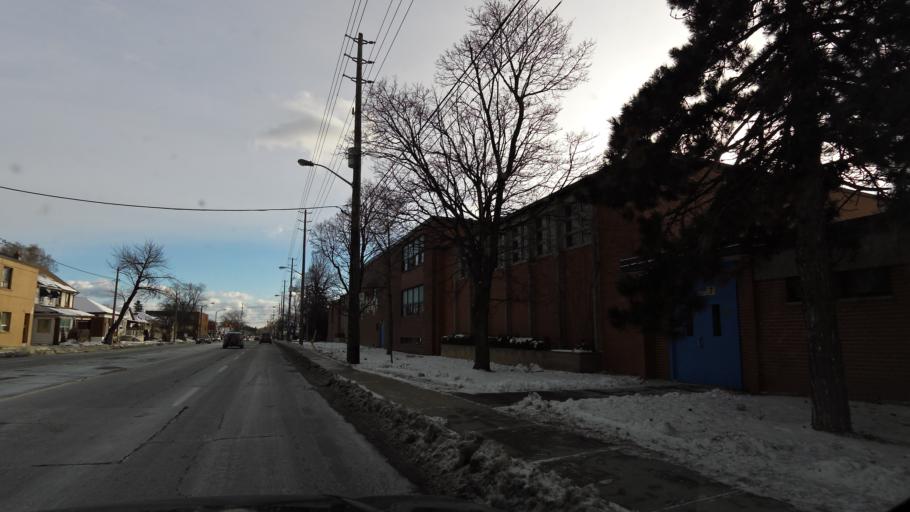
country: CA
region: Ontario
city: Etobicoke
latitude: 43.6023
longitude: -79.5187
